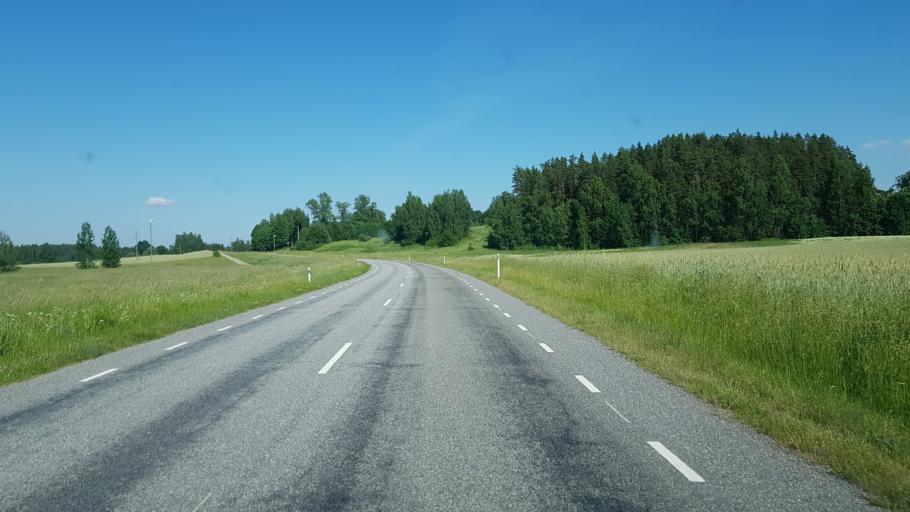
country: EE
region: Vorumaa
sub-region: Voru linn
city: Voru
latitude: 57.8578
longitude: 27.1223
